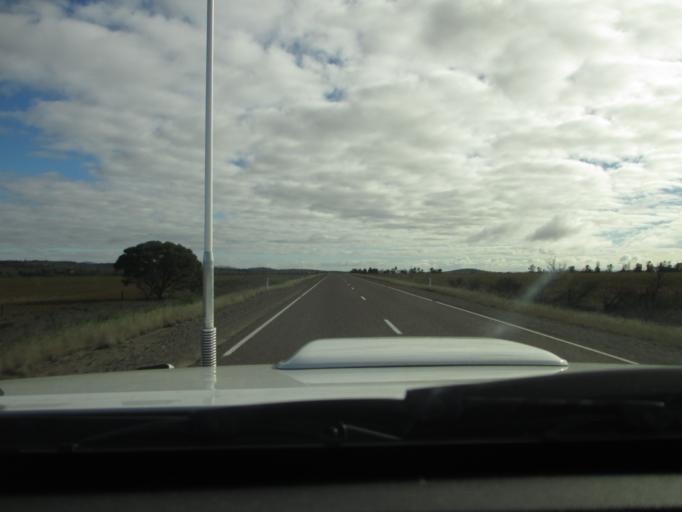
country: AU
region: South Australia
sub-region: Peterborough
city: Peterborough
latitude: -32.5391
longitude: 138.5580
